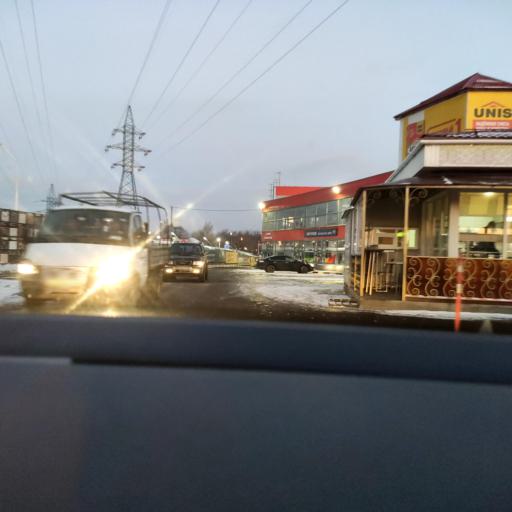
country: RU
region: Moskovskaya
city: Reutov
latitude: 55.7772
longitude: 37.8538
